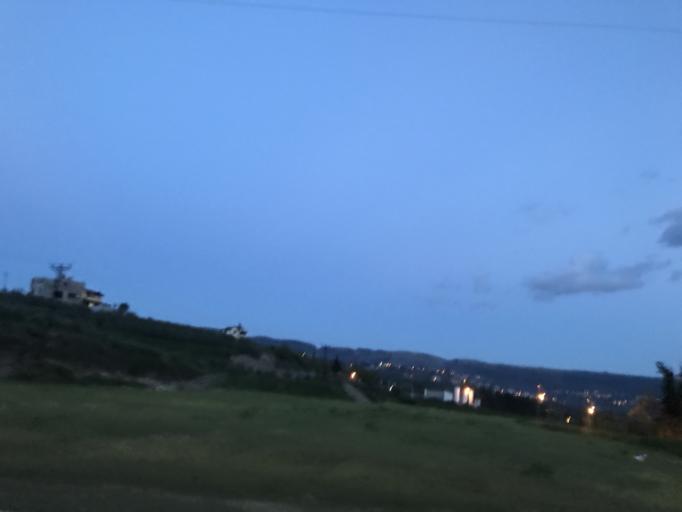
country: TR
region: Hatay
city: Samankaya
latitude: 36.1614
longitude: 36.0990
